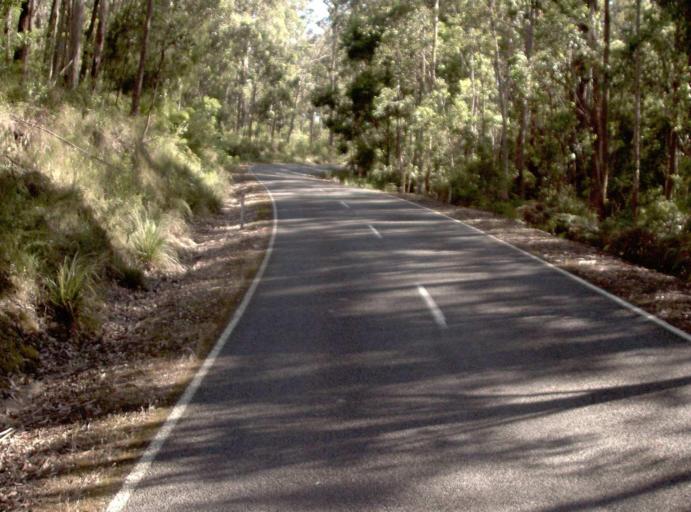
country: AU
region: Victoria
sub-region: East Gippsland
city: Lakes Entrance
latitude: -37.6309
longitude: 148.5037
